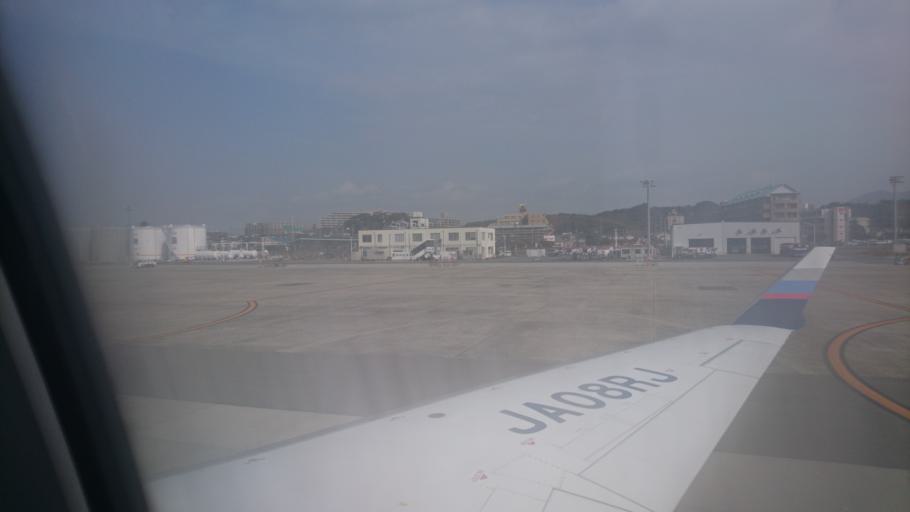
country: JP
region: Fukuoka
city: Fukuoka-shi
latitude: 33.5882
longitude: 130.4514
